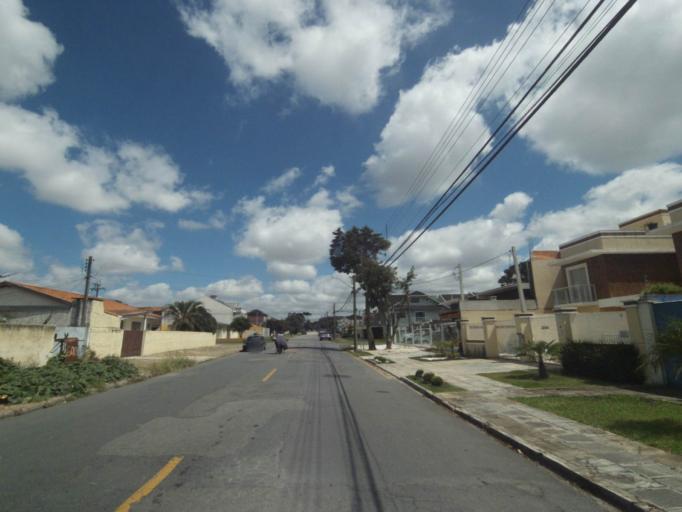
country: BR
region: Parana
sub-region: Pinhais
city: Pinhais
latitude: -25.4397
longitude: -49.2139
